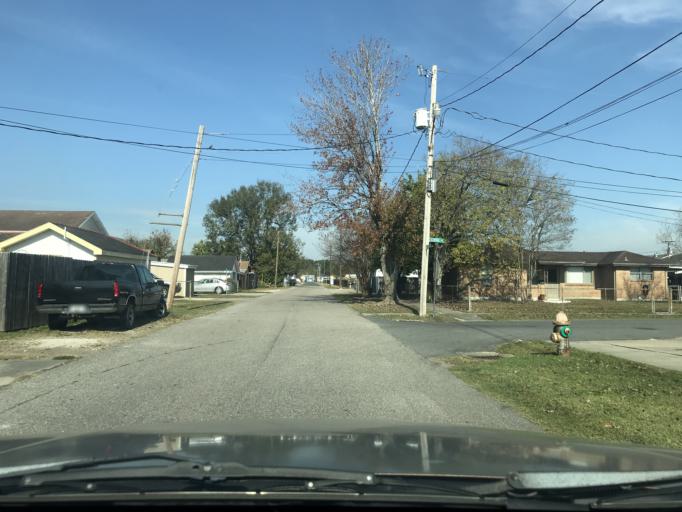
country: US
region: Louisiana
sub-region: Jefferson Parish
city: Marrero
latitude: 29.8966
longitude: -90.0919
